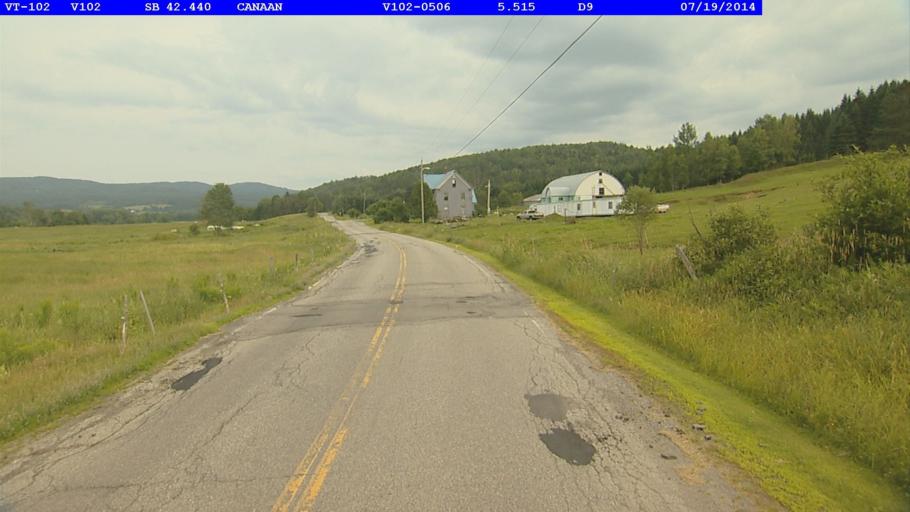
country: US
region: New Hampshire
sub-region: Coos County
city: Colebrook
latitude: 44.9785
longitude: -71.5414
